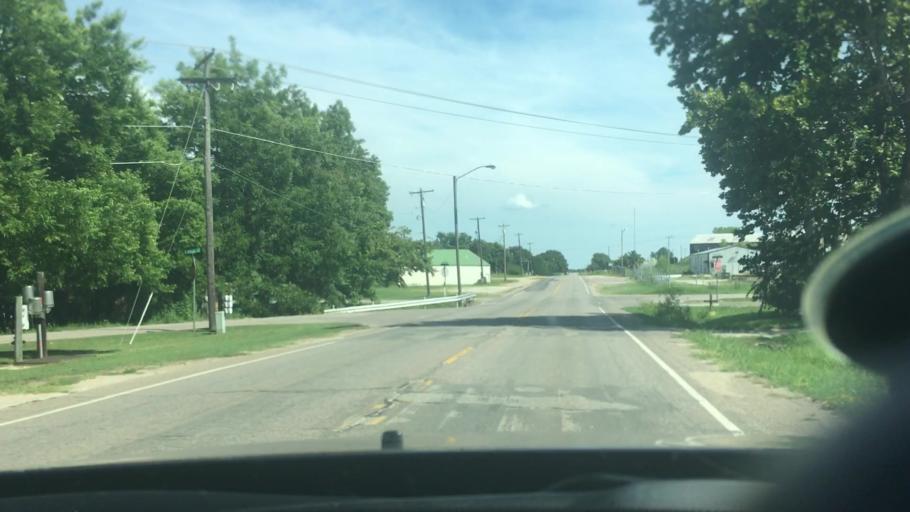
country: US
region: Oklahoma
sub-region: Seminole County
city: Seminole
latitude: 35.2343
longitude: -96.6892
